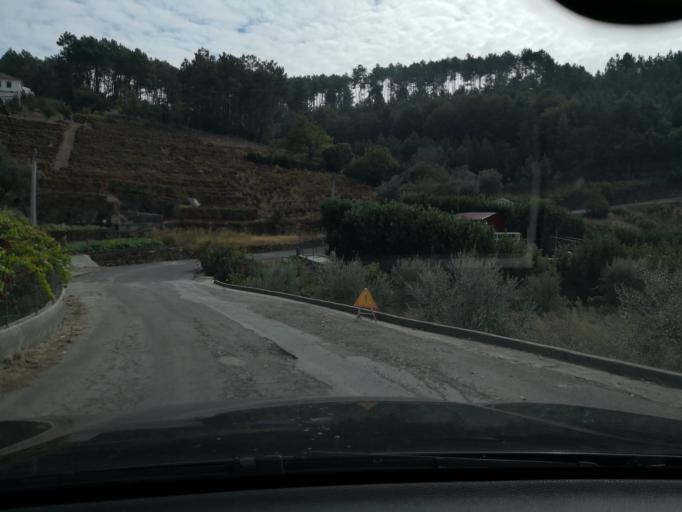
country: PT
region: Vila Real
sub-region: Sabrosa
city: Vilela
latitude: 41.2191
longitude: -7.6850
